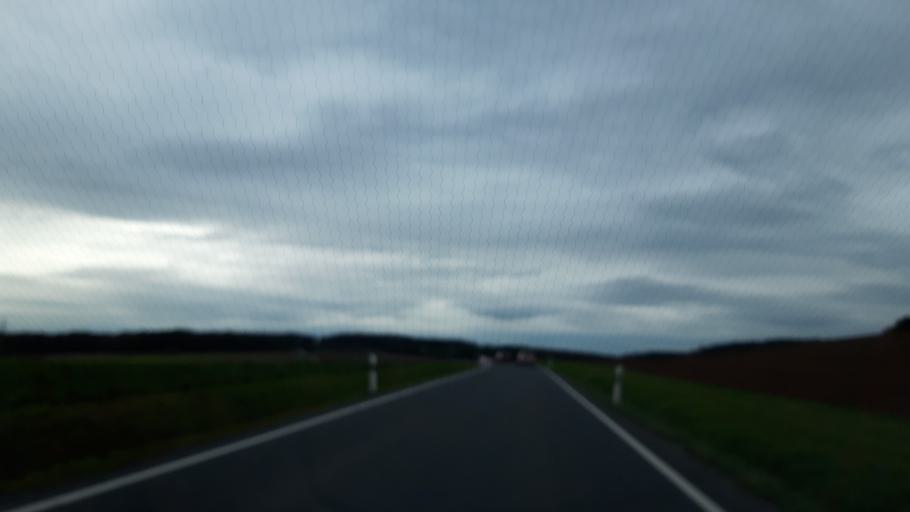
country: DE
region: Bavaria
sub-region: Regierungsbezirk Unterfranken
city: Marktheidenfeld
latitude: 49.7986
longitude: 9.5756
